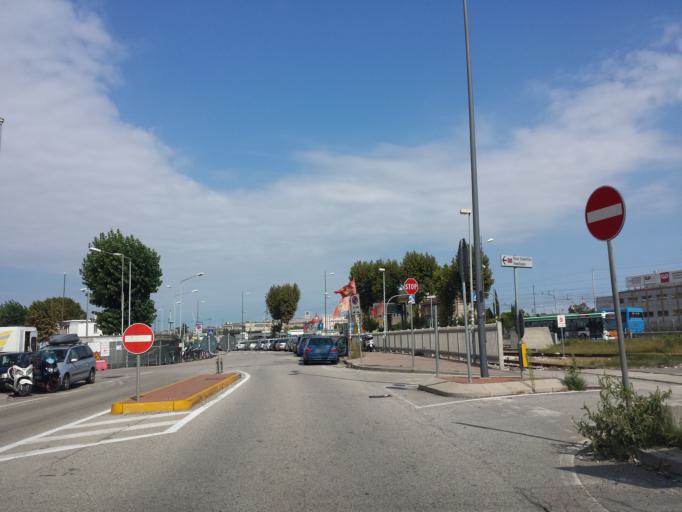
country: IT
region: Veneto
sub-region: Provincia di Venezia
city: Mestre
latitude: 45.4751
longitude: 12.2509
